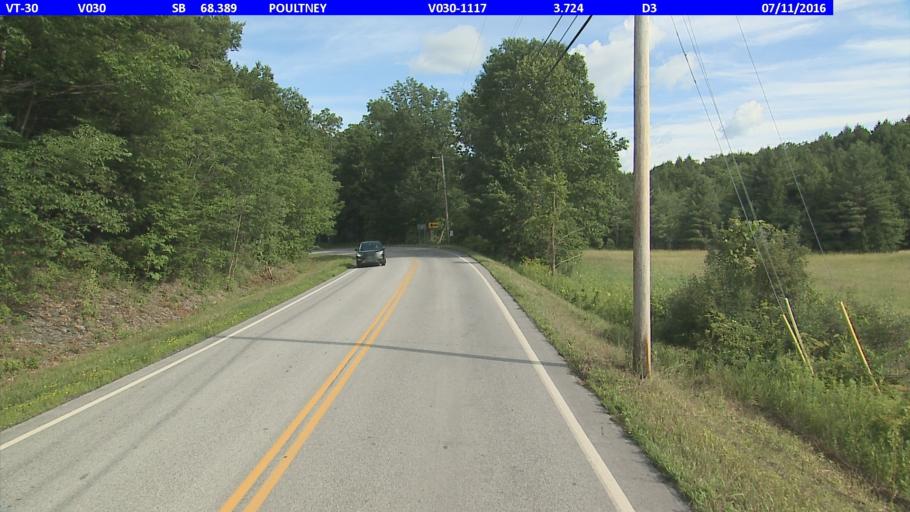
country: US
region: Vermont
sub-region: Rutland County
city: Poultney
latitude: 43.5114
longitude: -73.2206
